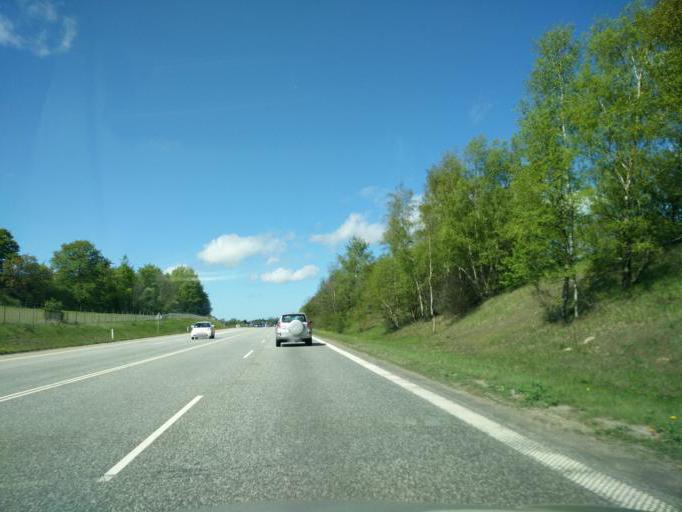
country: DK
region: Capital Region
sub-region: Hillerod Kommune
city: Hillerod
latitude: 55.9147
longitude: 12.2642
